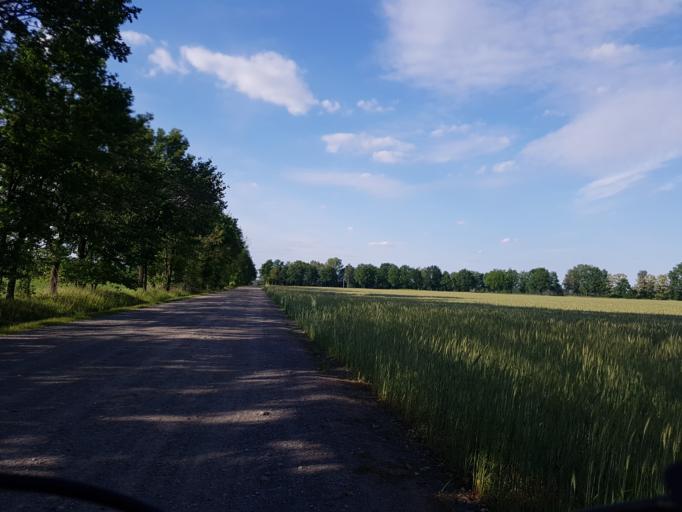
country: DE
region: Brandenburg
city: Elsterwerda
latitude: 51.4343
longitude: 13.5306
